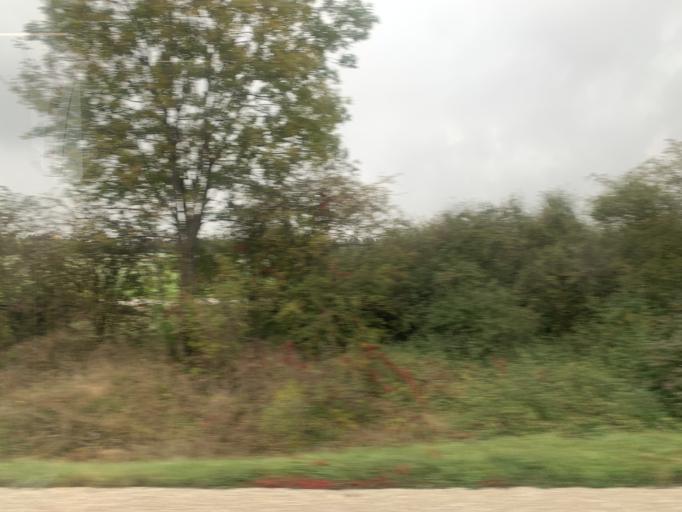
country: DE
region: Bavaria
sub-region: Upper Bavaria
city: Oberschleissheim
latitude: 48.2249
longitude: 11.5421
